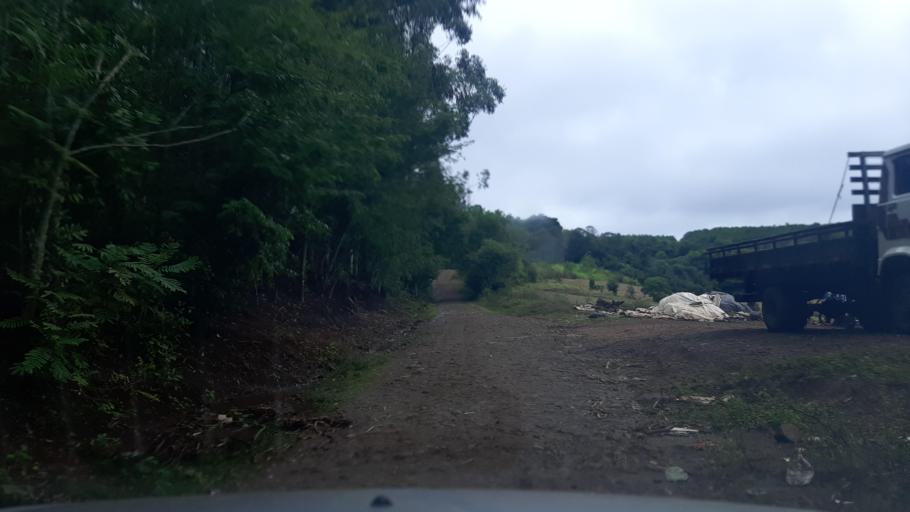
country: BR
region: Parana
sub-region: Ampere
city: Ampere
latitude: -26.0573
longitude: -53.5468
